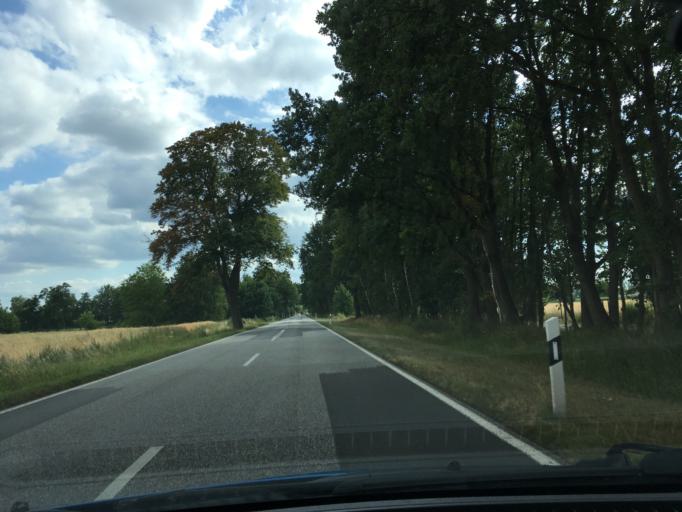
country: DE
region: Mecklenburg-Vorpommern
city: Lubtheen
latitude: 53.3411
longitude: 11.0806
